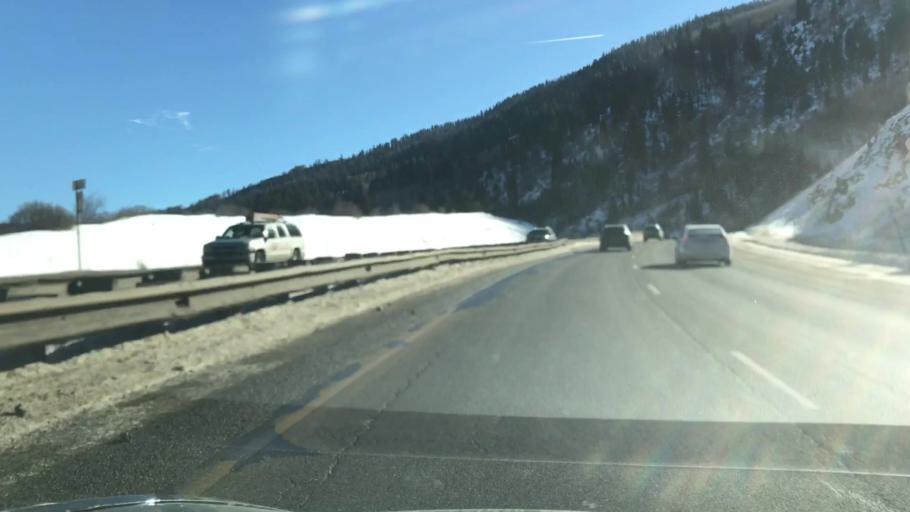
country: US
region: Colorado
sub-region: Eagle County
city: Minturn
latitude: 39.6144
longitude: -106.4594
